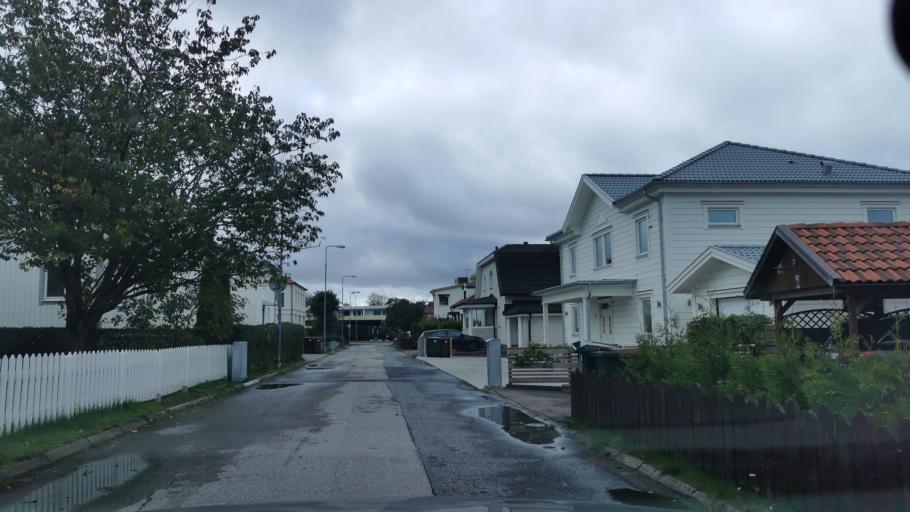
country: SE
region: Vaestra Goetaland
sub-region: Partille Kommun
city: Partille
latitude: 57.7314
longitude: 12.0718
